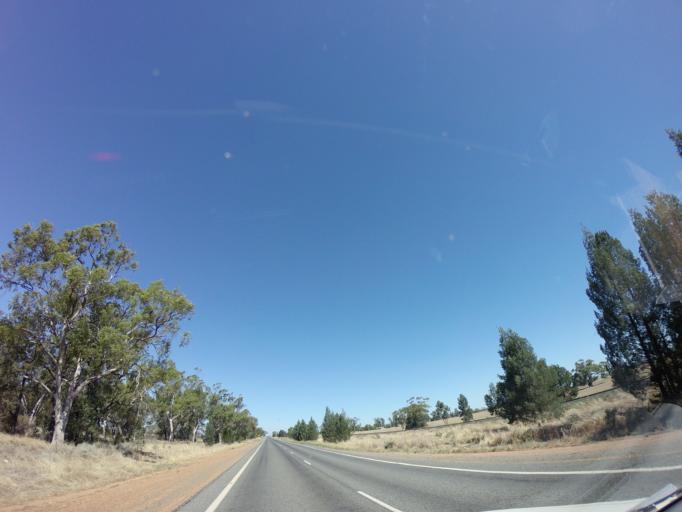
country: AU
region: New South Wales
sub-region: Bogan
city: Nyngan
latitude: -31.5771
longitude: 147.2250
